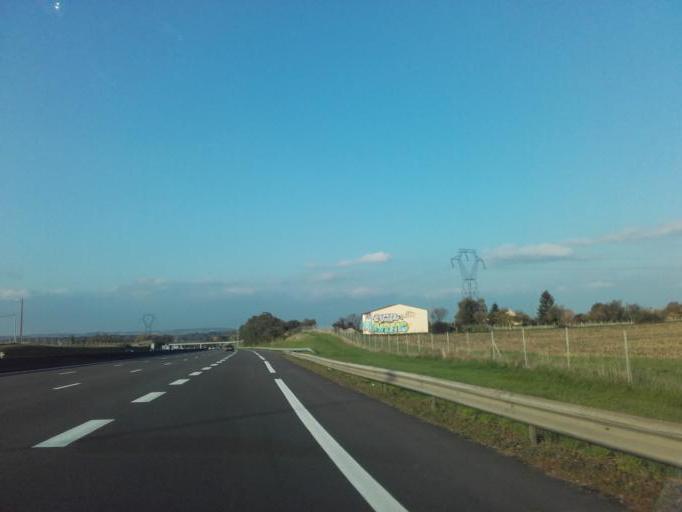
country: FR
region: Bourgogne
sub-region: Departement de Saone-et-Loire
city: Saint-Martin-Belle-Roche
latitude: 46.4233
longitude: 4.8672
